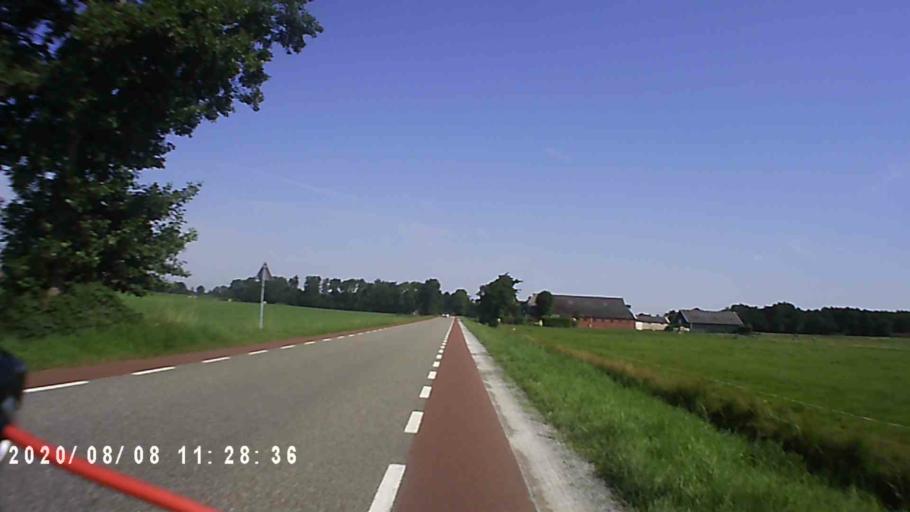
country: NL
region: Groningen
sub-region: Gemeente Leek
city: Leek
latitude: 53.1928
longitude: 6.3862
